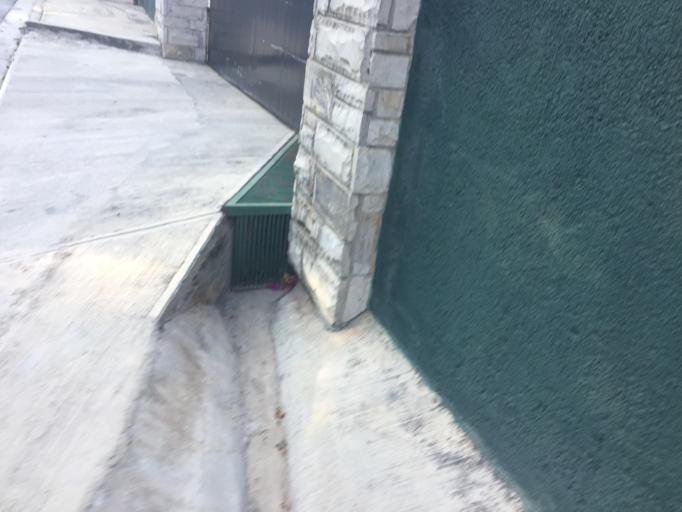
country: MX
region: Nuevo Leon
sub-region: San Pedro Garza Garcia
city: San Pedro Garza Garcia
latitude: 25.6571
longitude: -100.3983
